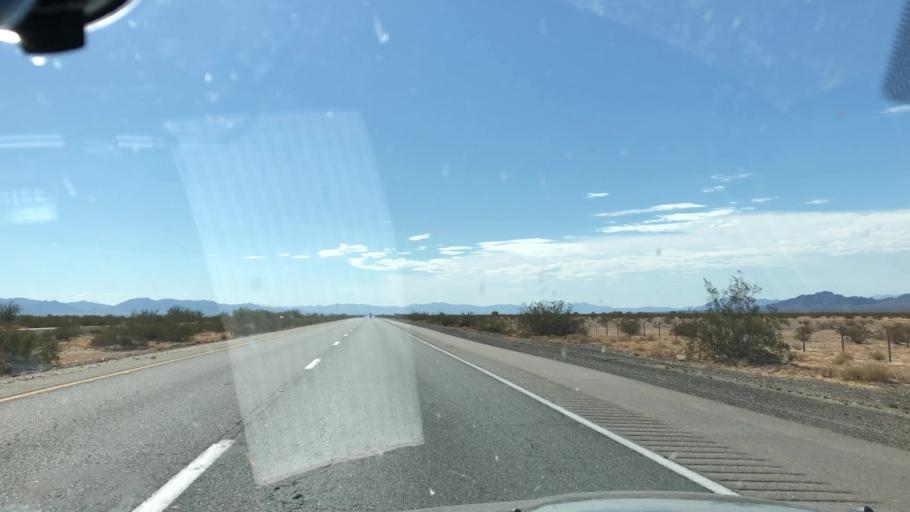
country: US
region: California
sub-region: Riverside County
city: Mesa Verde
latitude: 33.6129
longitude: -115.0080
